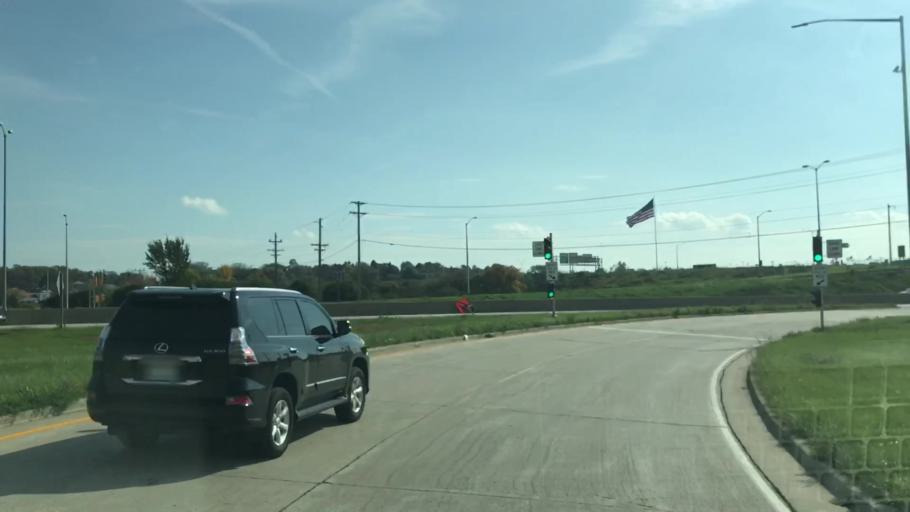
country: US
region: Wisconsin
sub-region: Waukesha County
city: Butler
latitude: 43.1487
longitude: -88.0556
